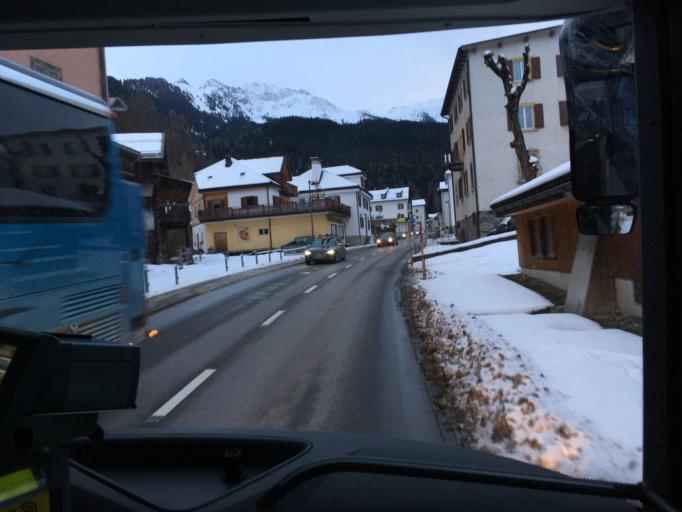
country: CH
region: Grisons
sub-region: Albula District
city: Tiefencastel
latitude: 46.5822
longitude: 9.6184
